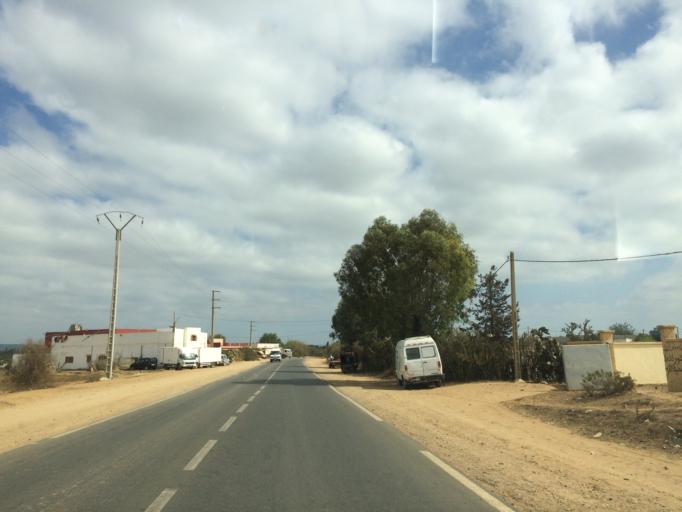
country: MA
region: Gharb-Chrarda-Beni Hssen
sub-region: Kenitra Province
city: Lalla Mimouna
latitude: 34.8438
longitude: -6.1626
